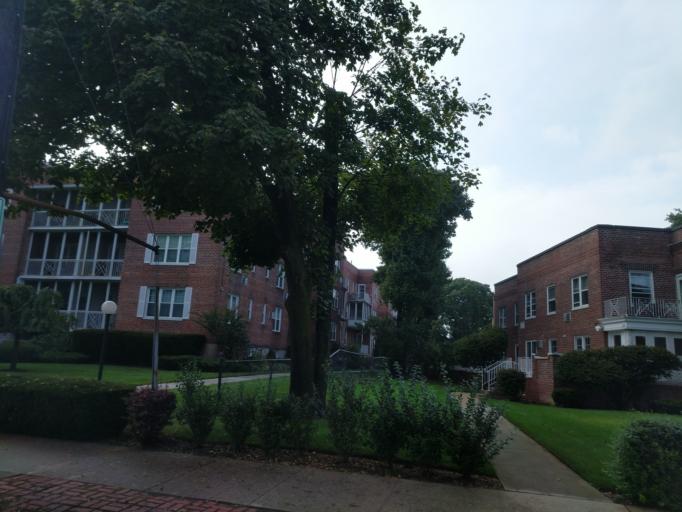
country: US
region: New York
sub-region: Nassau County
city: Lawrence
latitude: 40.6153
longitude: -73.7339
